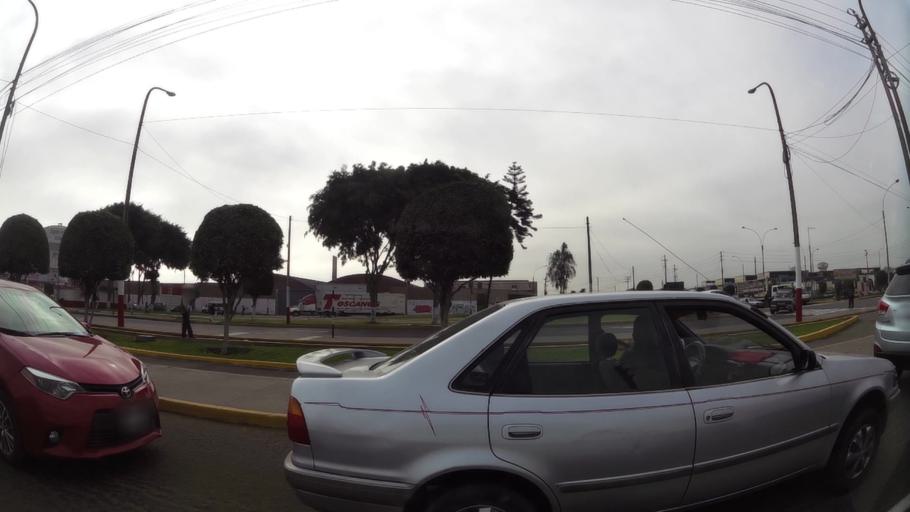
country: PE
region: Callao
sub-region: Callao
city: Callao
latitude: -12.0199
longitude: -77.1016
